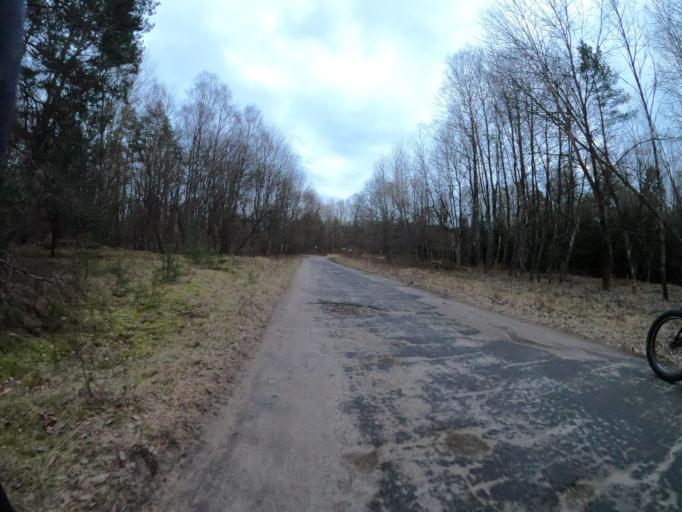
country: PL
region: West Pomeranian Voivodeship
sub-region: Powiat szczecinecki
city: Borne Sulinowo
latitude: 53.5443
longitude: 16.5845
